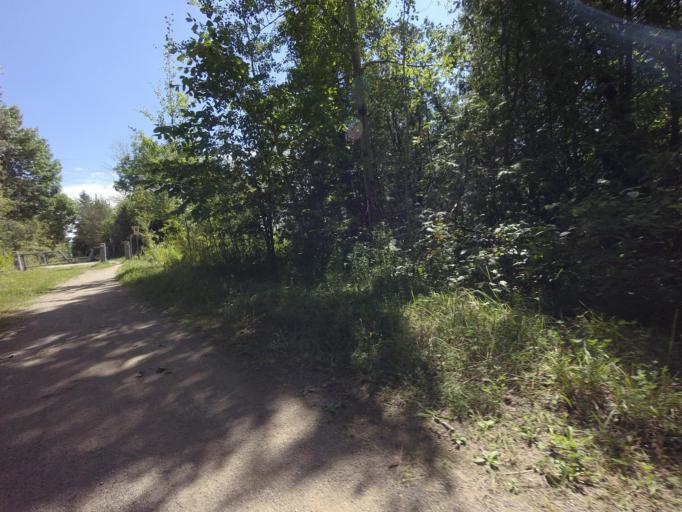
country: CA
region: Ontario
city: Orangeville
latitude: 43.7756
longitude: -80.1990
